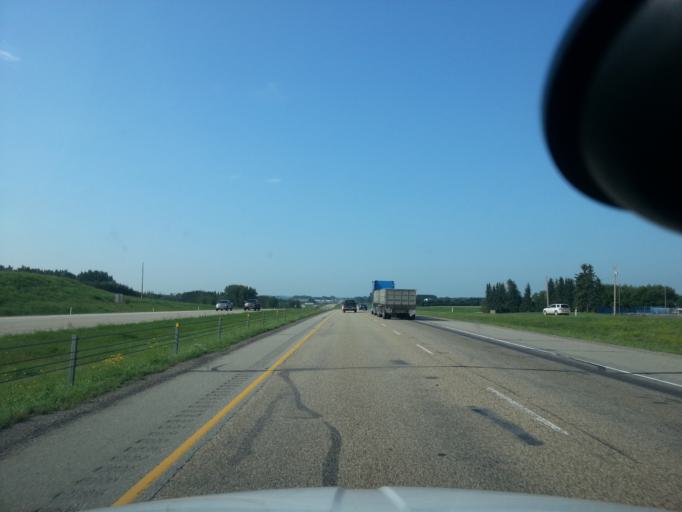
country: CA
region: Alberta
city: Penhold
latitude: 52.0008
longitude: -113.9649
